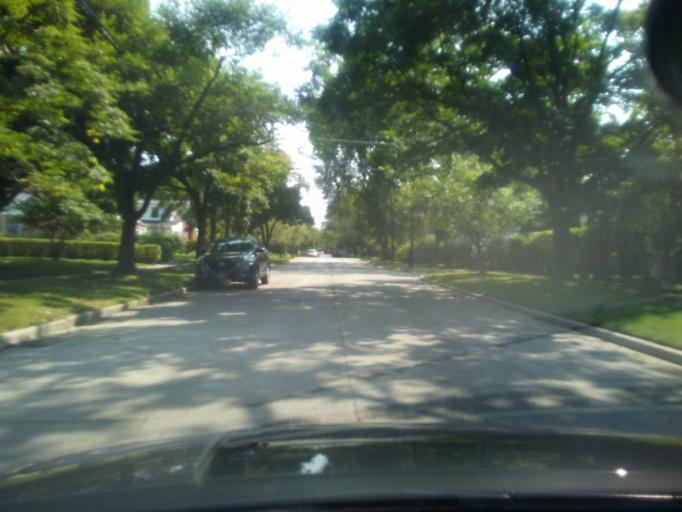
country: US
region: Illinois
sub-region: Cook County
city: Evanston
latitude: 42.0249
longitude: -87.6944
